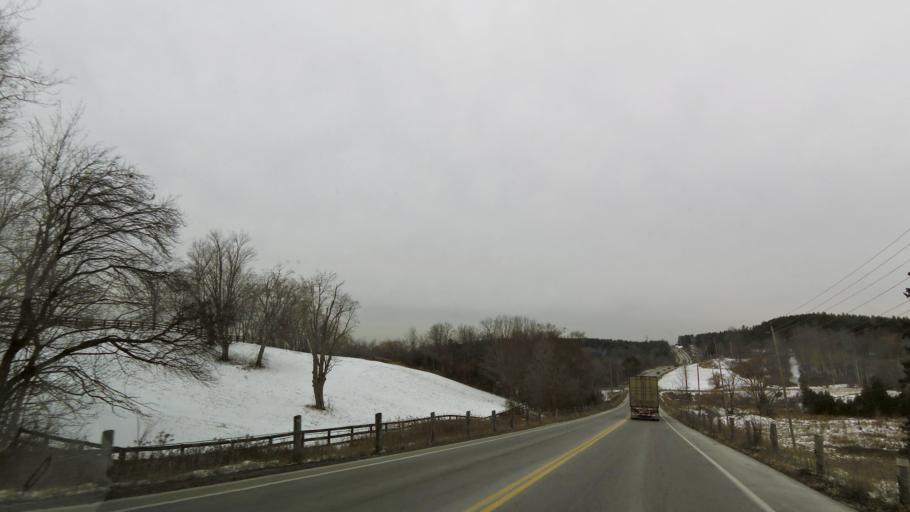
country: CA
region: Ontario
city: Vaughan
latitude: 43.9128
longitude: -79.6002
